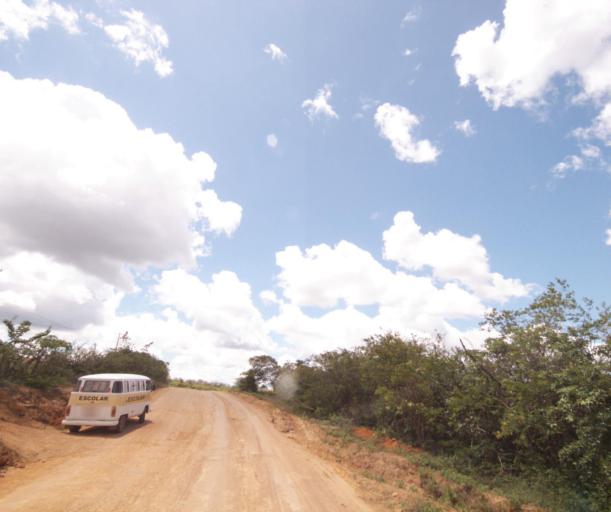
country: BR
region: Bahia
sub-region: Pocoes
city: Pocoes
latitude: -14.3860
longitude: -40.5524
